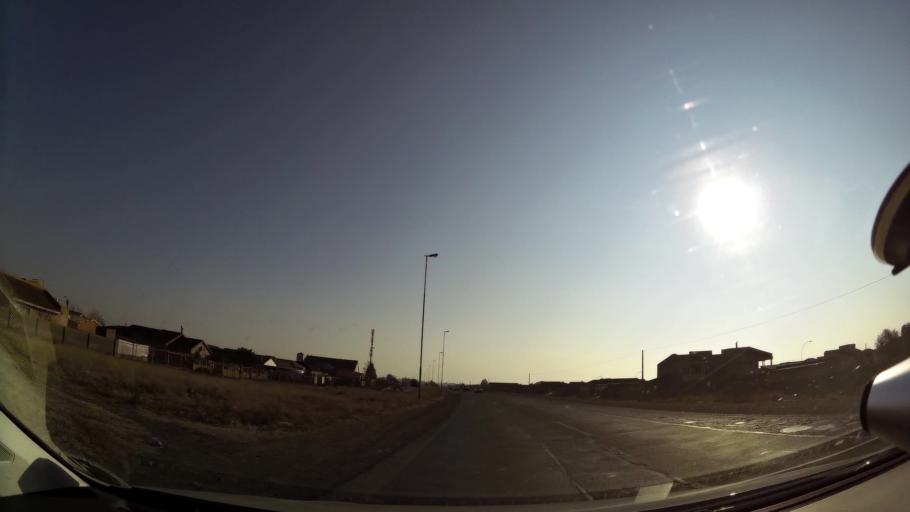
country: ZA
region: Orange Free State
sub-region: Mangaung Metropolitan Municipality
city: Bloemfontein
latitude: -29.1534
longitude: 26.2649
